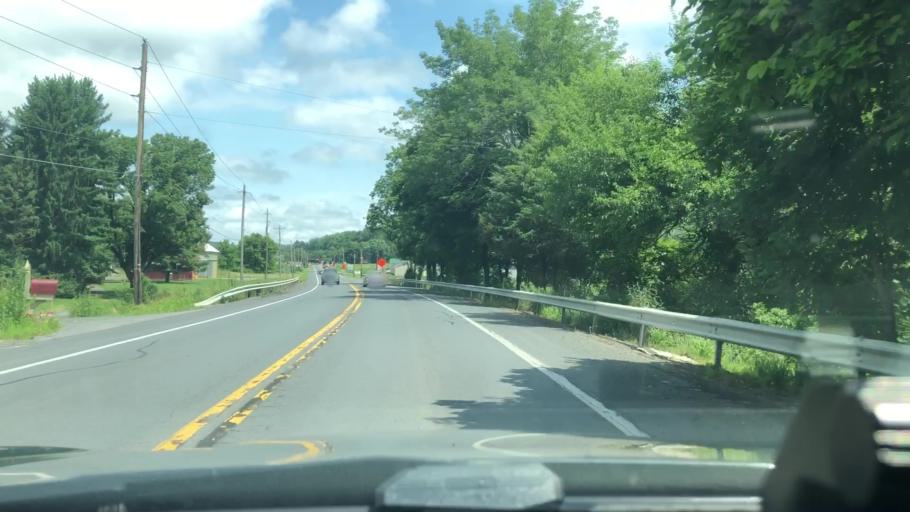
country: US
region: Pennsylvania
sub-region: Berks County
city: Bally
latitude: 40.4422
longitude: -75.5551
